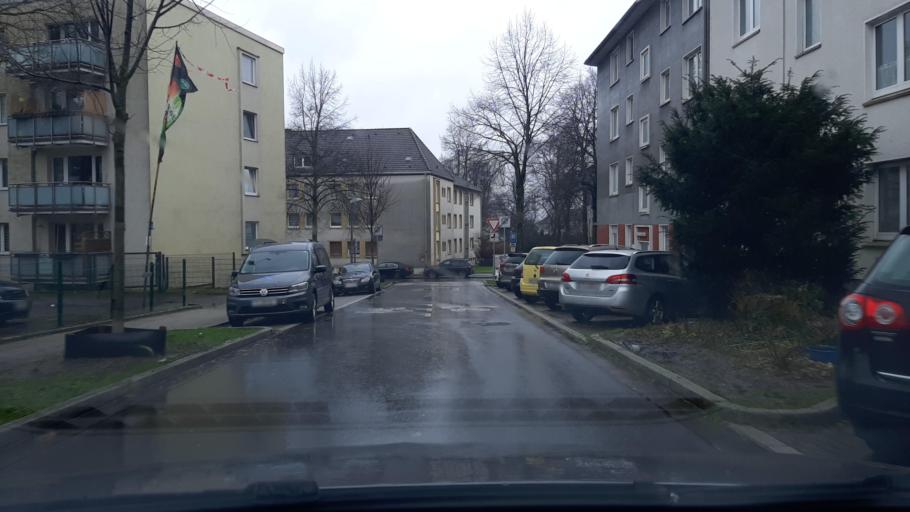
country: DE
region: North Rhine-Westphalia
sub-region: Regierungsbezirk Dusseldorf
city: Essen
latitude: 51.4413
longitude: 6.9863
